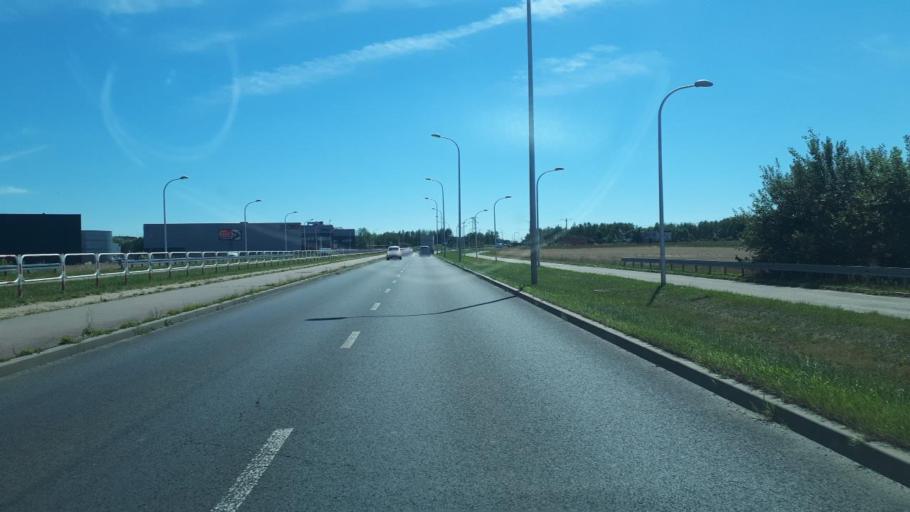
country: PL
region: Silesian Voivodeship
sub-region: Tychy
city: Cielmice
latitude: 50.1060
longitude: 19.0497
